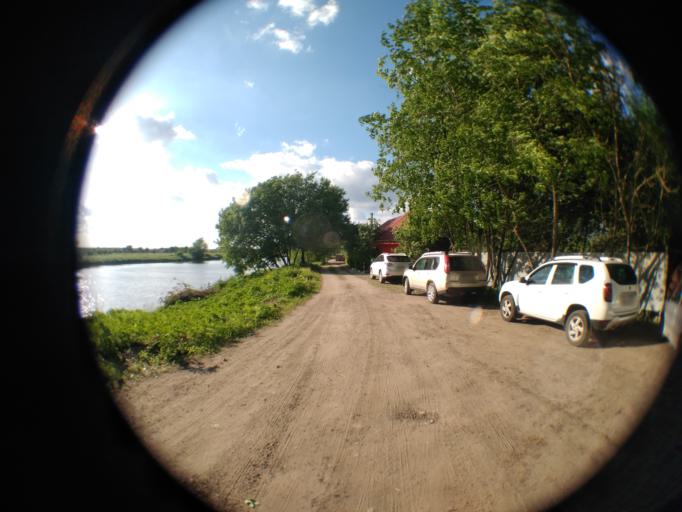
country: RU
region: Moskovskaya
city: Zhukovskiy
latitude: 55.5754
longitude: 38.1039
